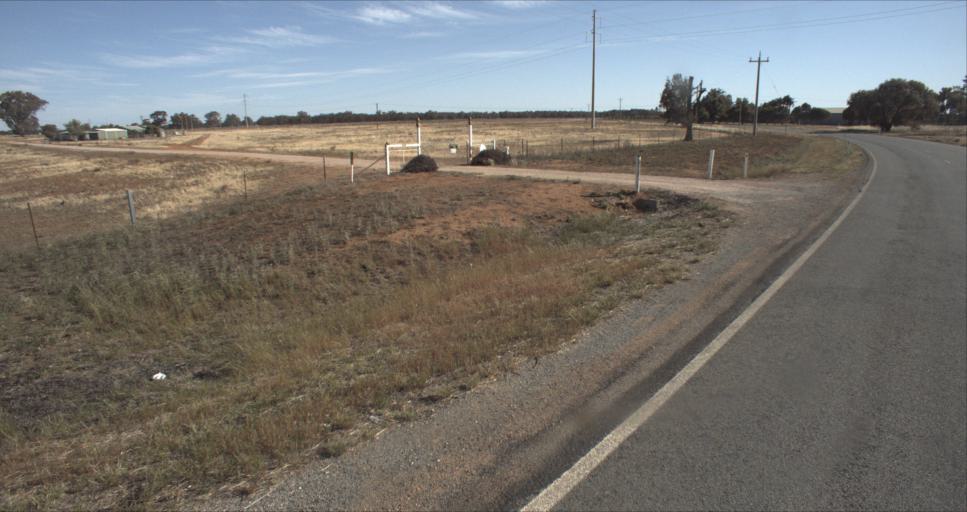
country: AU
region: New South Wales
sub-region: Leeton
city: Leeton
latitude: -34.6090
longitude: 146.4058
